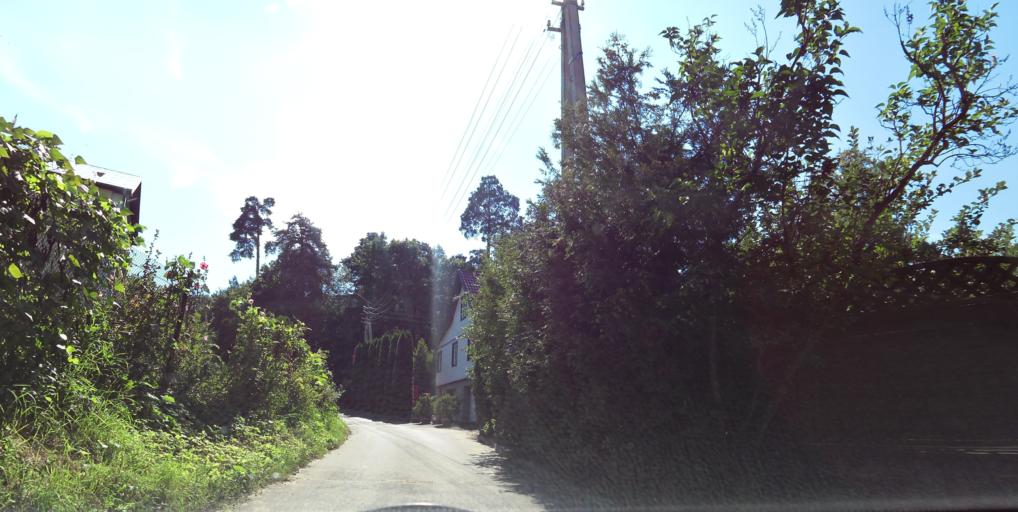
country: LT
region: Vilnius County
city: Rasos
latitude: 54.6922
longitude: 25.3121
